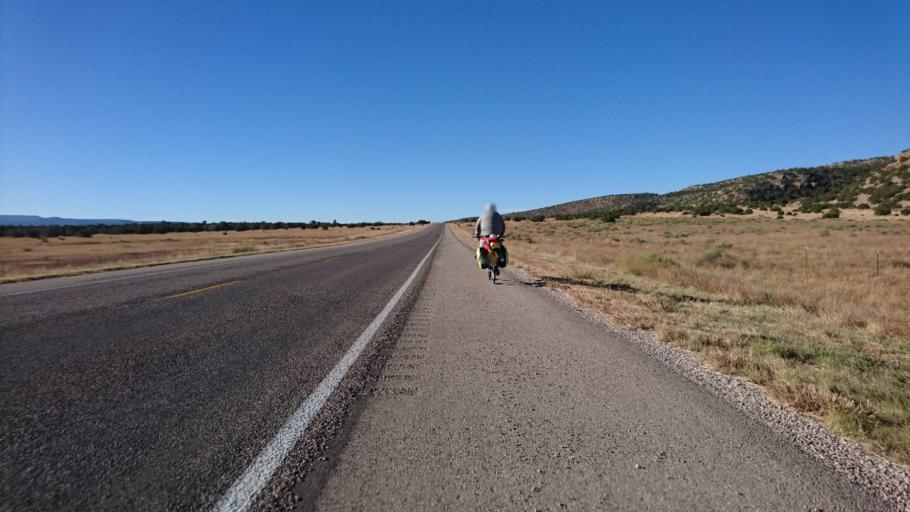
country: US
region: New Mexico
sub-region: Cibola County
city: Grants
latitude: 34.9847
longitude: -107.9040
